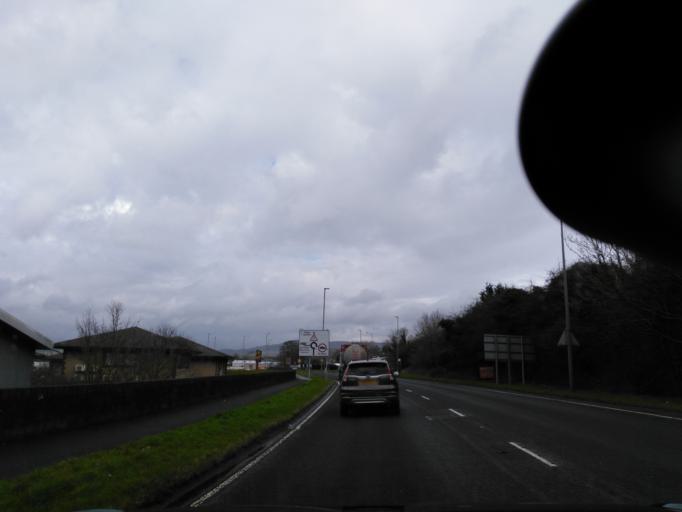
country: GB
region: England
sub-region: North Yorkshire
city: Skipton
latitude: 53.9392
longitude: -2.0123
